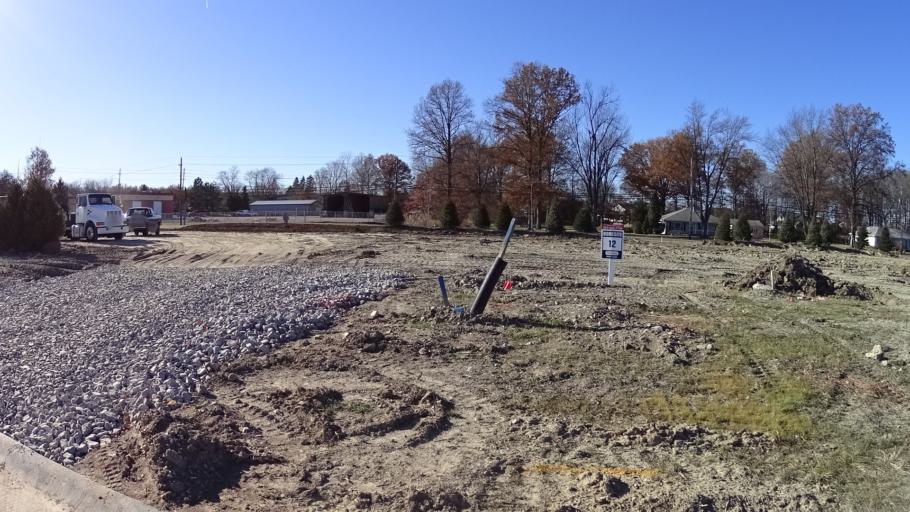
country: US
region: Ohio
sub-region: Lorain County
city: Avon Center
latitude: 41.4554
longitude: -81.9992
